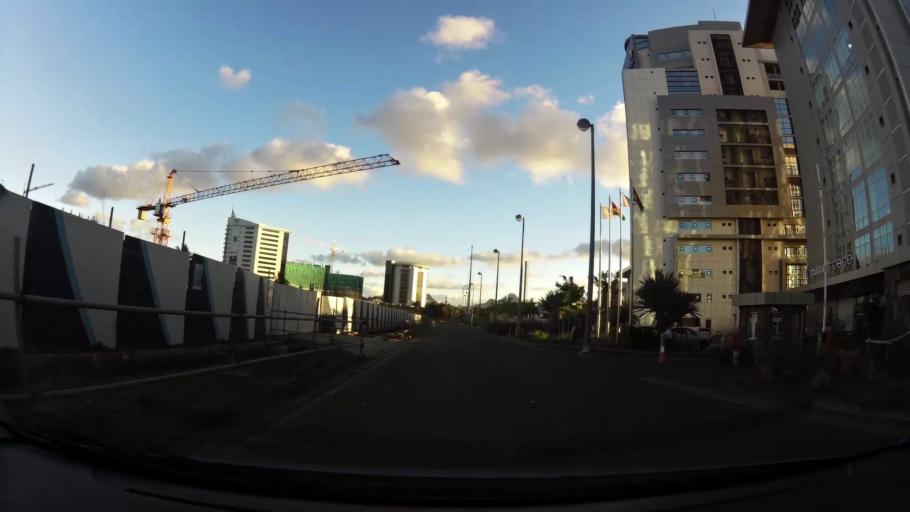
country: MU
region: Plaines Wilhems
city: Ebene
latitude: -20.2447
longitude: 57.4939
